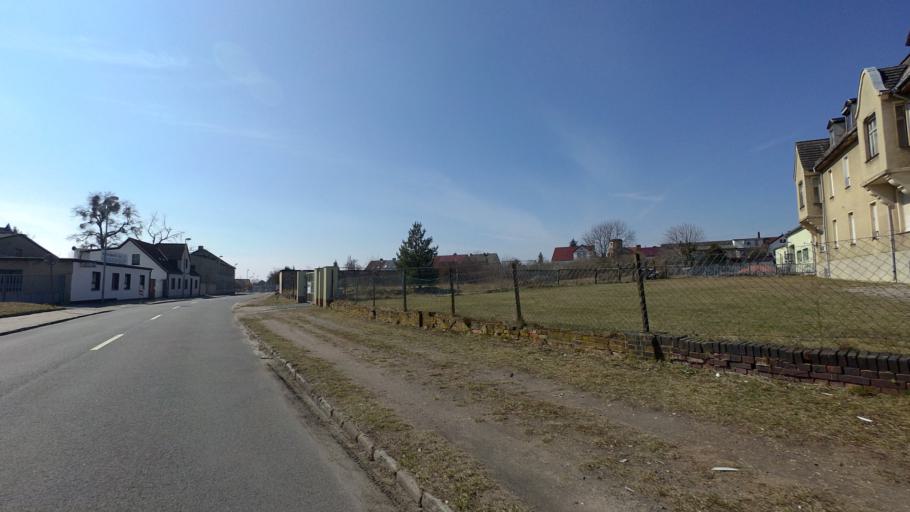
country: DE
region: Saxony-Anhalt
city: Coswig
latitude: 51.8896
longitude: 12.4625
